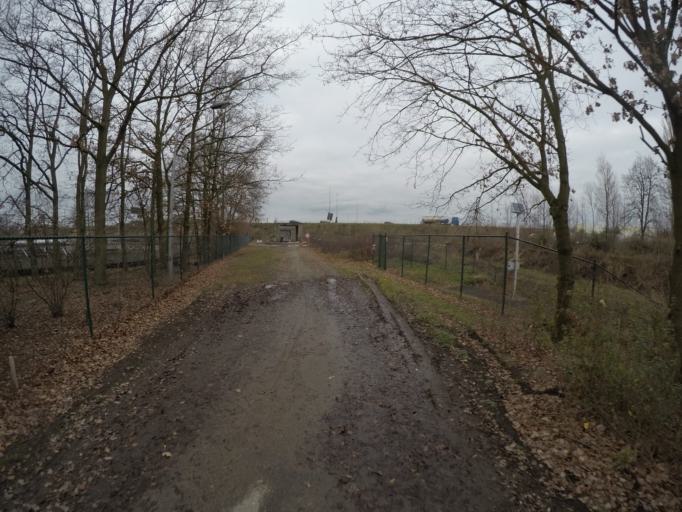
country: BE
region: Flanders
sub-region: Provincie Antwerpen
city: Zwijndrecht
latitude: 51.2122
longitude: 4.3500
